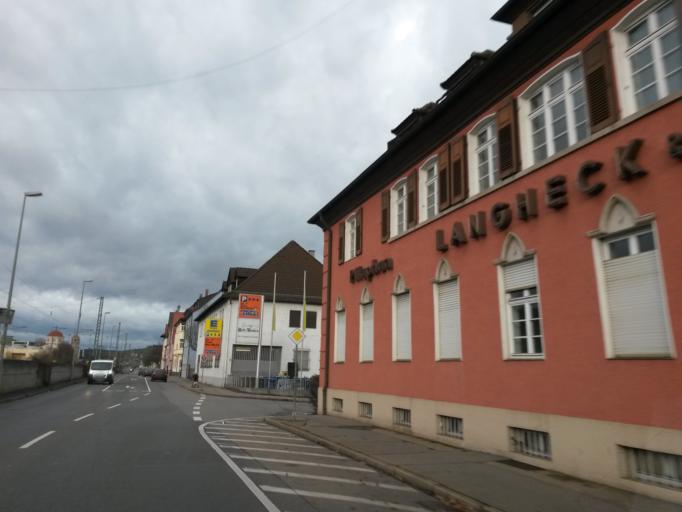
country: DE
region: Baden-Wuerttemberg
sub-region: Regierungsbezirk Stuttgart
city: Esslingen
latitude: 48.7328
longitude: 9.3191
